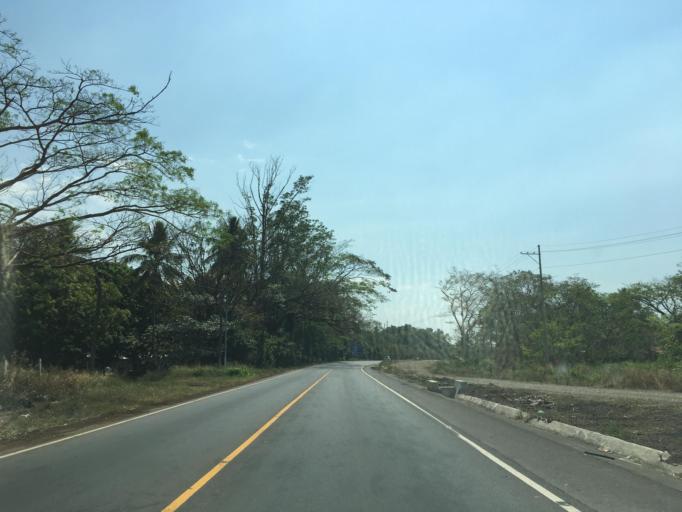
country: GT
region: Escuintla
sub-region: Municipio de Escuintla
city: Escuintla
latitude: 14.2720
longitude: -90.7560
